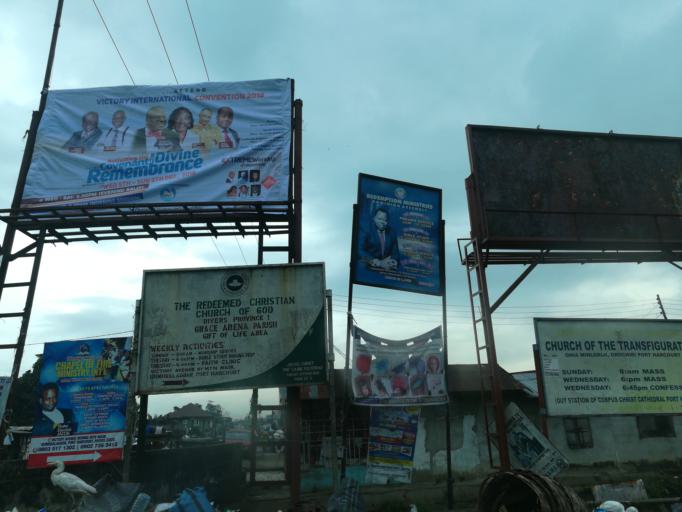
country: NG
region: Rivers
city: Port Harcourt
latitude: 4.8142
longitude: 7.0157
